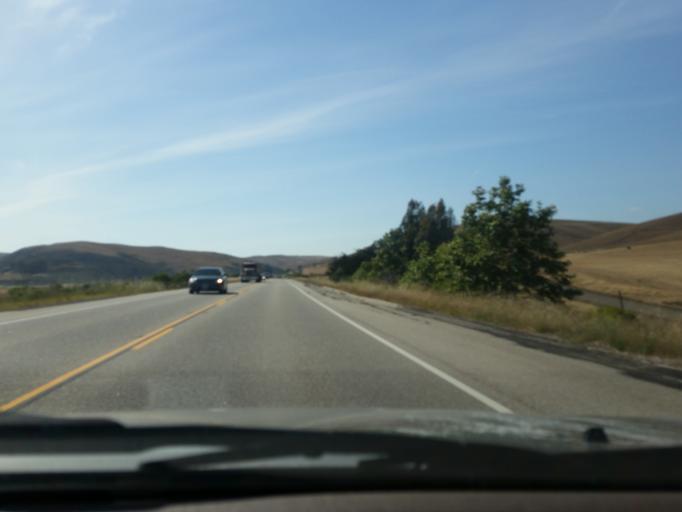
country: US
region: California
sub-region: San Luis Obispo County
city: Cayucos
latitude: 35.4560
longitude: -120.9565
